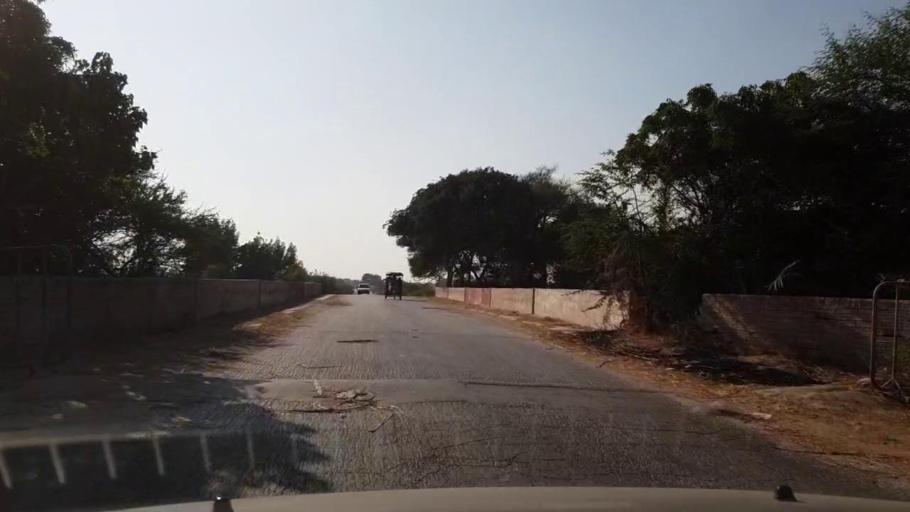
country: PK
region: Sindh
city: Tando Muhammad Khan
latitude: 25.0801
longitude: 68.4910
